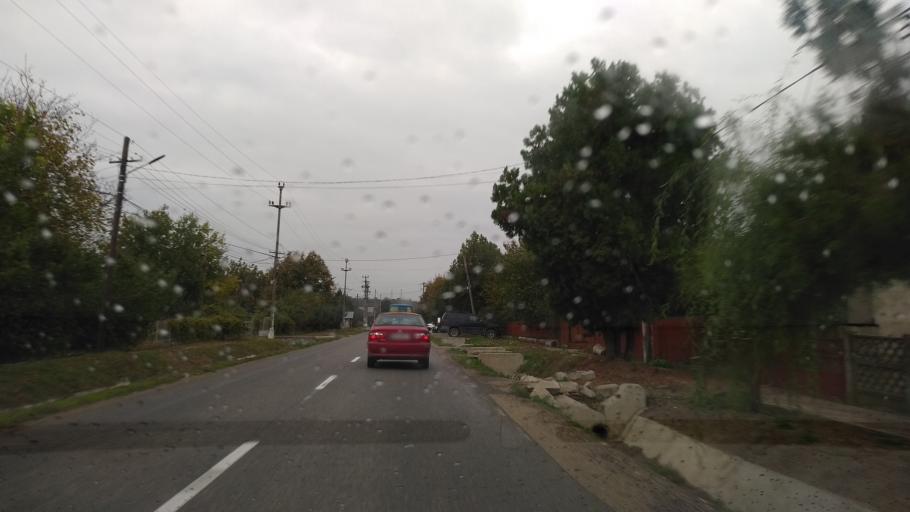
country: RO
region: Giurgiu
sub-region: Comuna Hotarele
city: Hotarele
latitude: 44.1838
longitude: 26.3680
